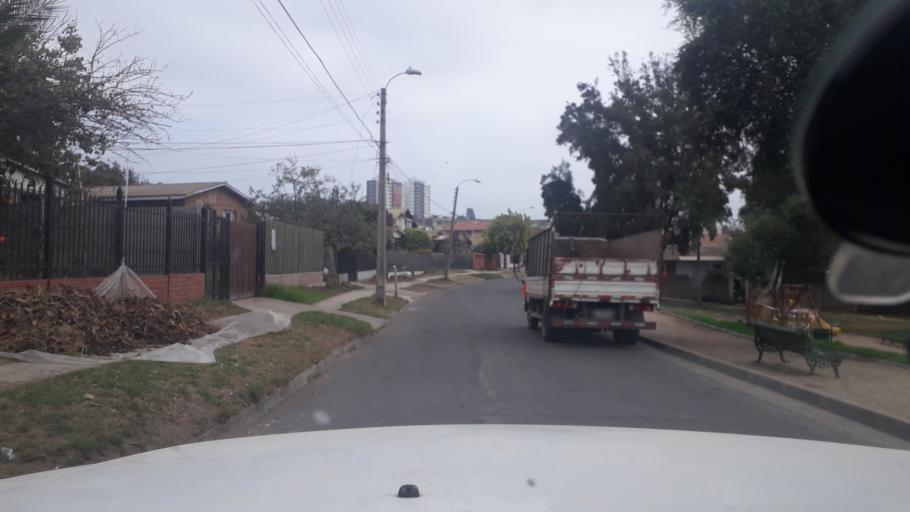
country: CL
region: Valparaiso
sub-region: Provincia de Valparaiso
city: Vina del Mar
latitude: -32.9355
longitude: -71.5247
